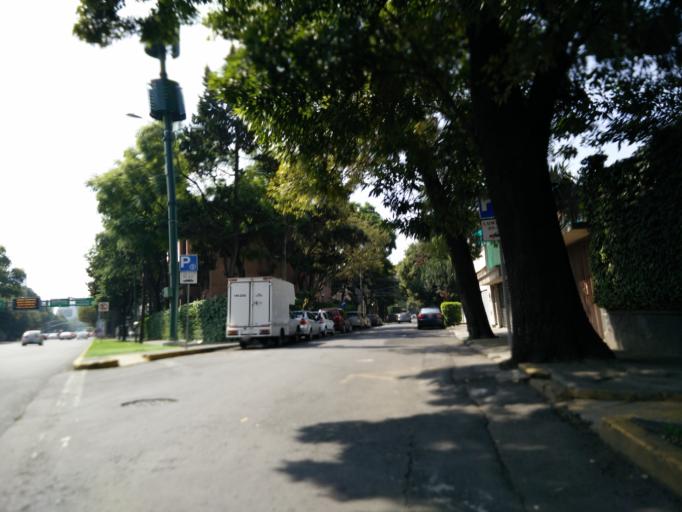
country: MX
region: Mexico City
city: Miguel Hidalgo
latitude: 19.4338
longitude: -99.1793
